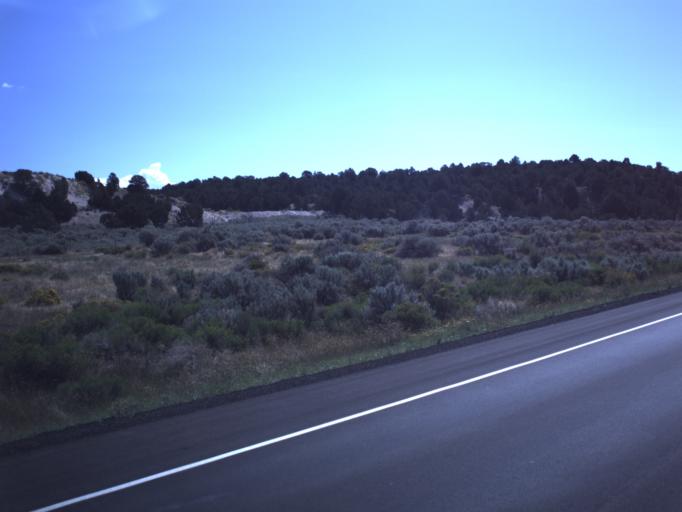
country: US
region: Utah
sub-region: Utah County
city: Eagle Mountain
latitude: 39.9858
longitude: -112.2639
